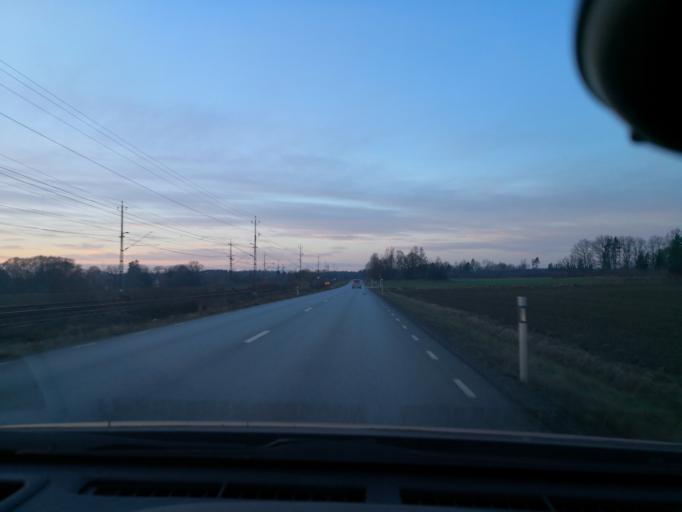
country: SE
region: Vaestmanland
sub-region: Arboga Kommun
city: Arboga
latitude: 59.4075
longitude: 15.7982
